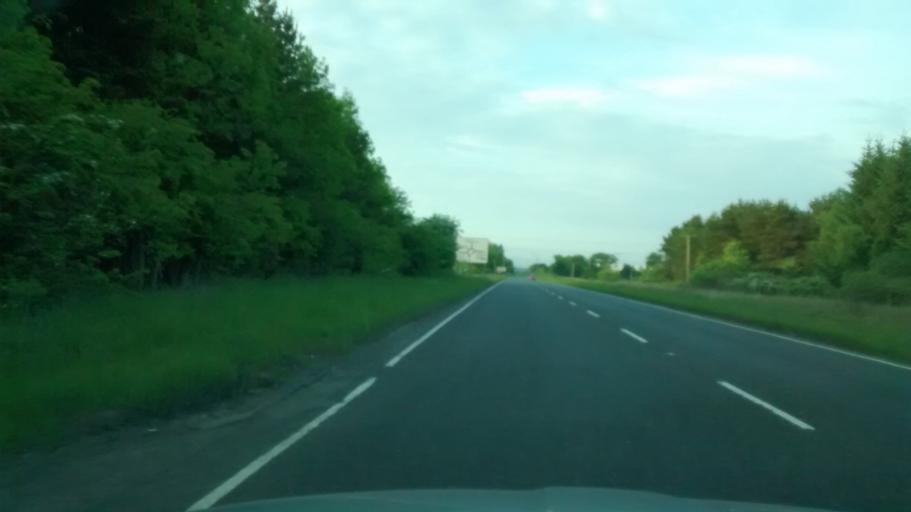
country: GB
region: Scotland
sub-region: West Lothian
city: Whitburn
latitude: 55.8782
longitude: -3.6671
